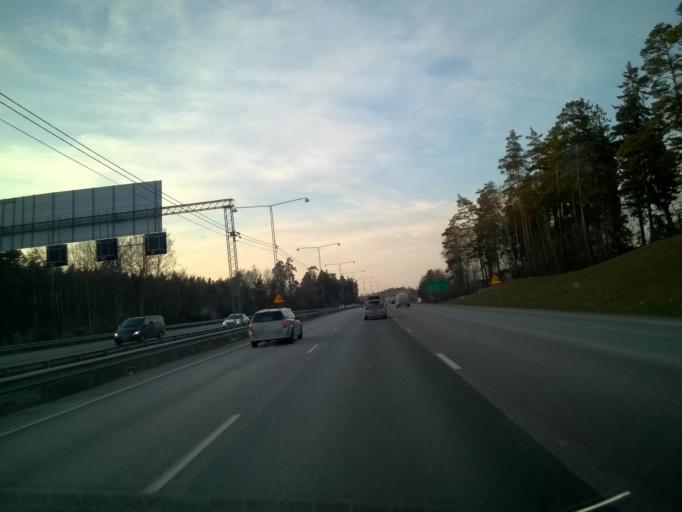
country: SE
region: Stockholm
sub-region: Sollentuna Kommun
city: Sollentuna
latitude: 59.4447
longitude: 17.9213
